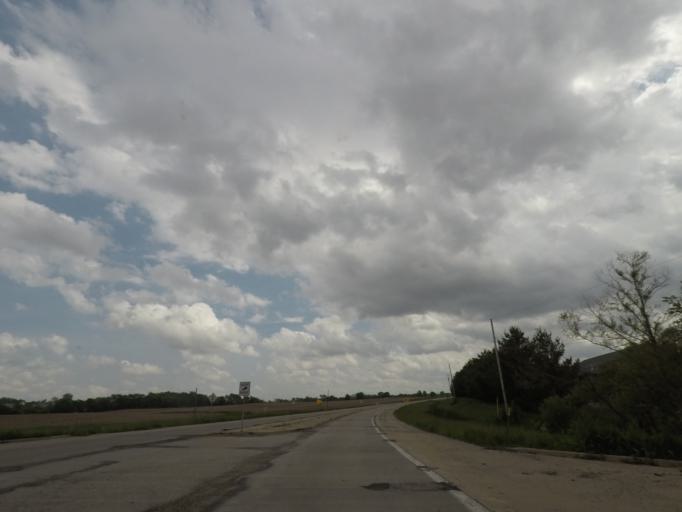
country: US
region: Illinois
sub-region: De Witt County
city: Clinton
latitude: 40.1731
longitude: -88.9611
